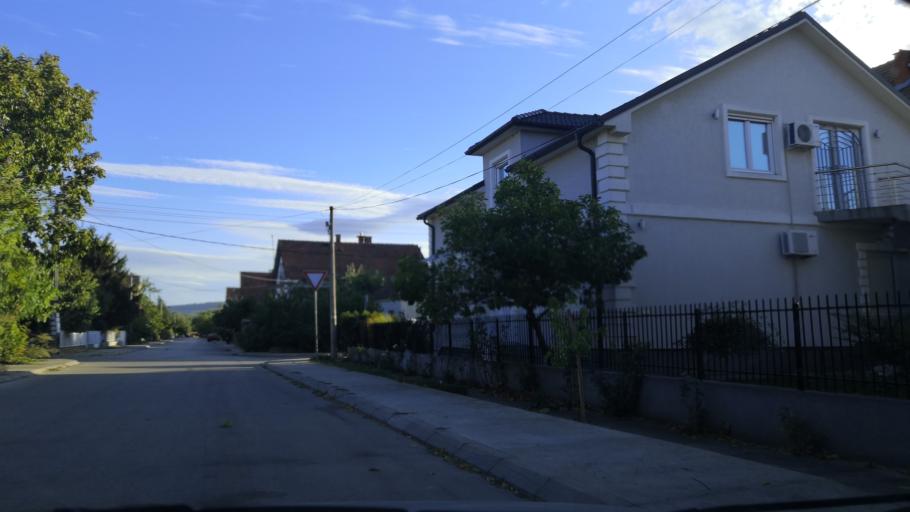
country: RS
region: Central Serbia
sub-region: Borski Okrug
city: Negotin
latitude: 44.2252
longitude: 22.5234
